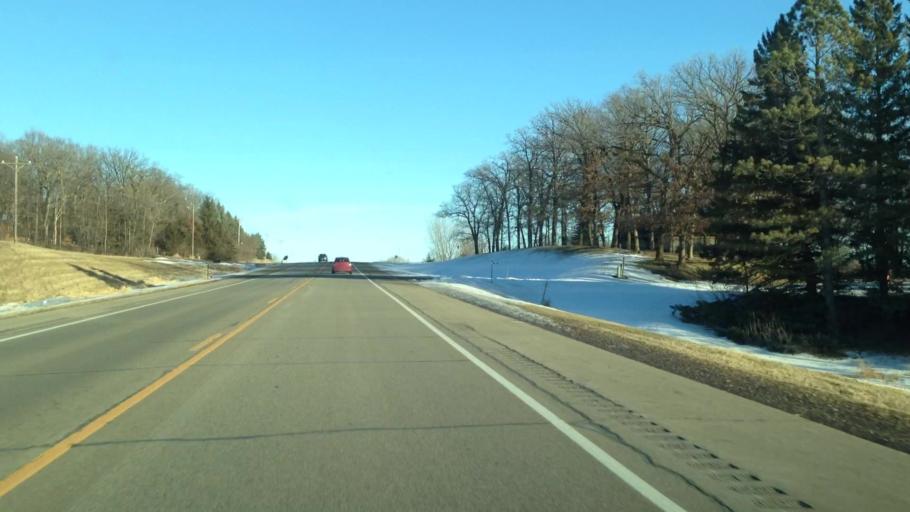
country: US
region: Minnesota
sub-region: Rice County
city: Lonsdale
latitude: 44.4791
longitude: -93.3648
